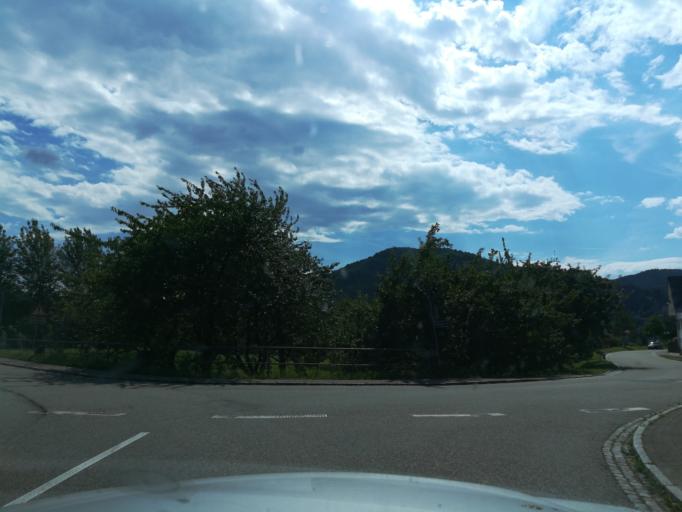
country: DE
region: Baden-Wuerttemberg
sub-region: Freiburg Region
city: Hofstetten
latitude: 48.2819
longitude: 8.0896
